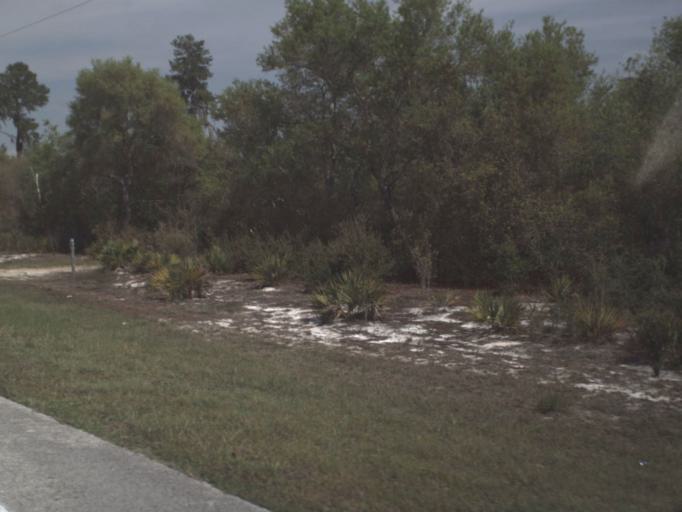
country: US
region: Florida
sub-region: Putnam County
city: Crescent City
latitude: 29.3115
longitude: -81.6884
